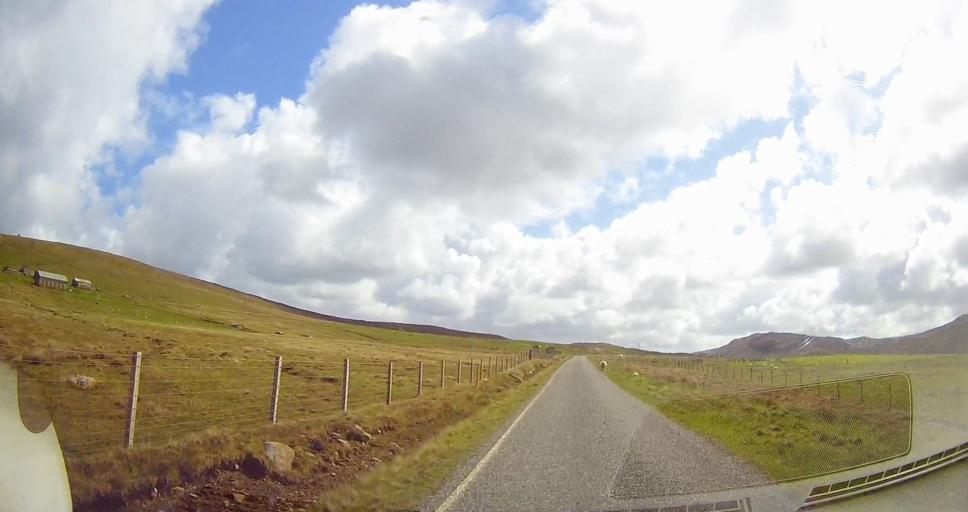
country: GB
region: Scotland
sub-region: Shetland Islands
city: Lerwick
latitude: 60.5685
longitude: -1.3329
